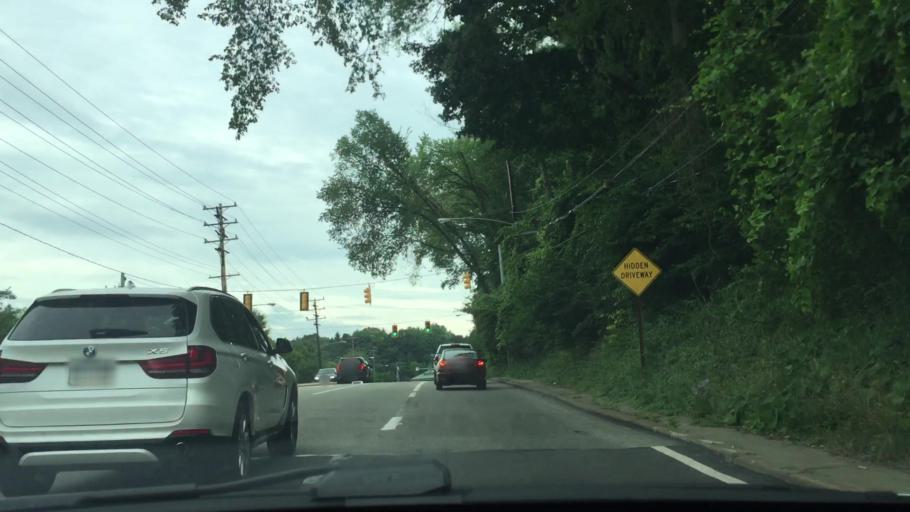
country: US
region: Pennsylvania
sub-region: Allegheny County
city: Mount Lebanon
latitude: 40.3569
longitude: -80.0540
